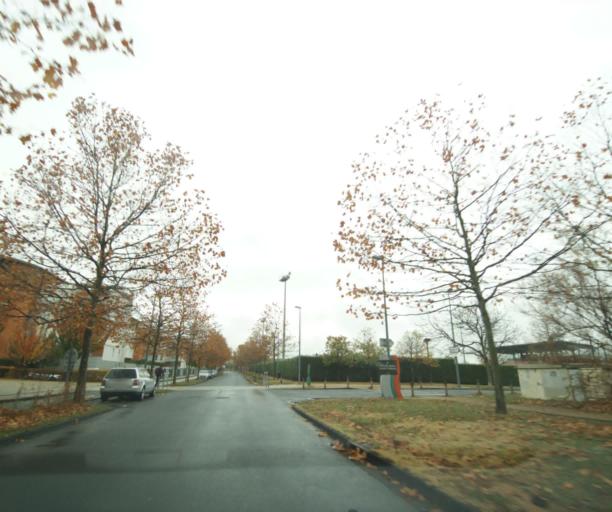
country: FR
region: Auvergne
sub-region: Departement du Puy-de-Dome
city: Cournon-d'Auvergne
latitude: 45.7412
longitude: 3.2101
